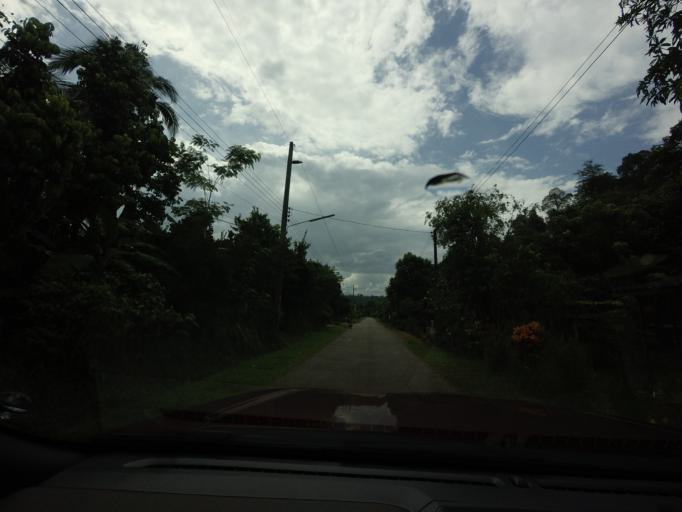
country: TH
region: Narathiwat
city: Sukhirin
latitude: 5.9216
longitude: 101.6419
